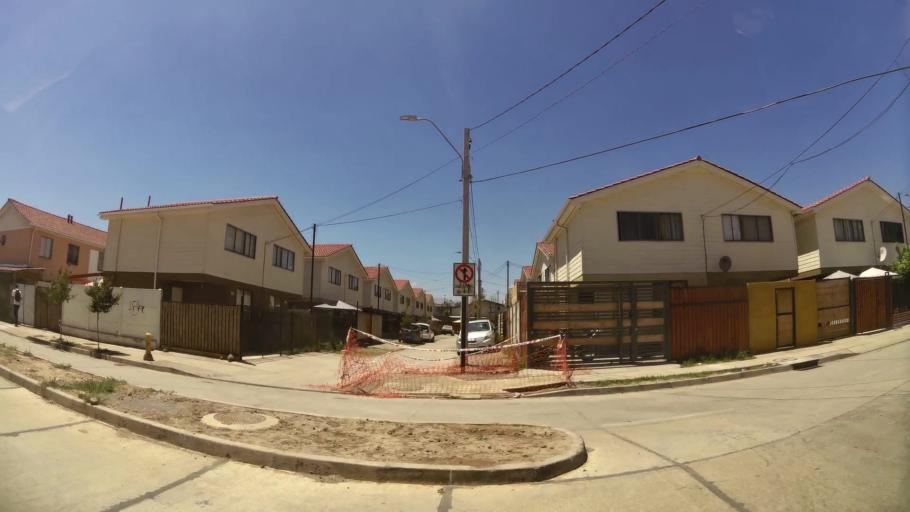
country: CL
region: Santiago Metropolitan
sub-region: Provincia de Maipo
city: San Bernardo
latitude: -33.6184
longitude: -70.7082
